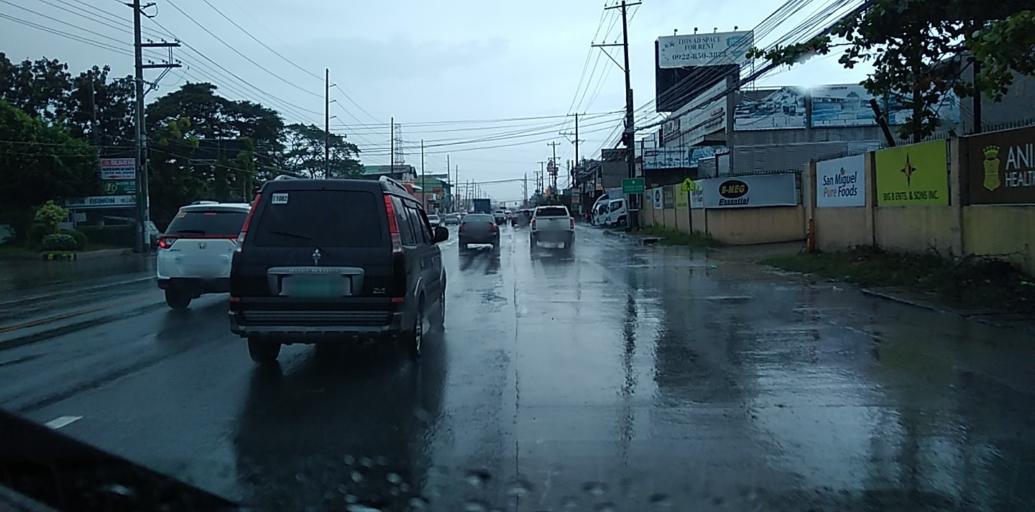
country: PH
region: Central Luzon
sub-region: Province of Pampanga
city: Magliman
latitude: 15.0471
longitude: 120.6691
